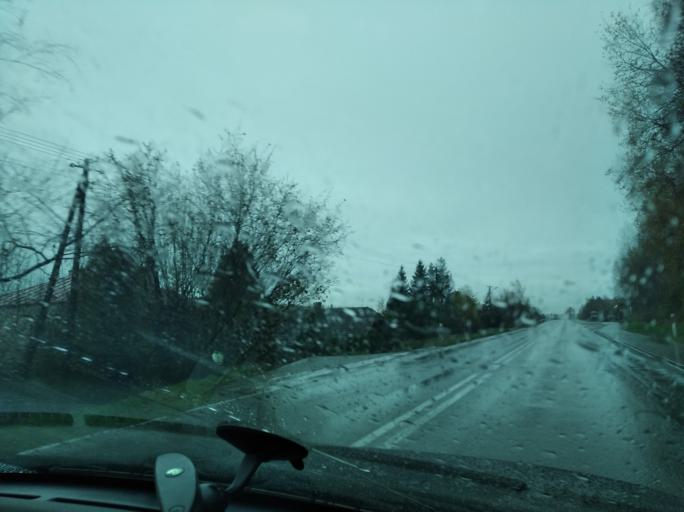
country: PL
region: Subcarpathian Voivodeship
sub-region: Powiat rzeszowski
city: Chmielnik
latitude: 49.9429
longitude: 22.1025
